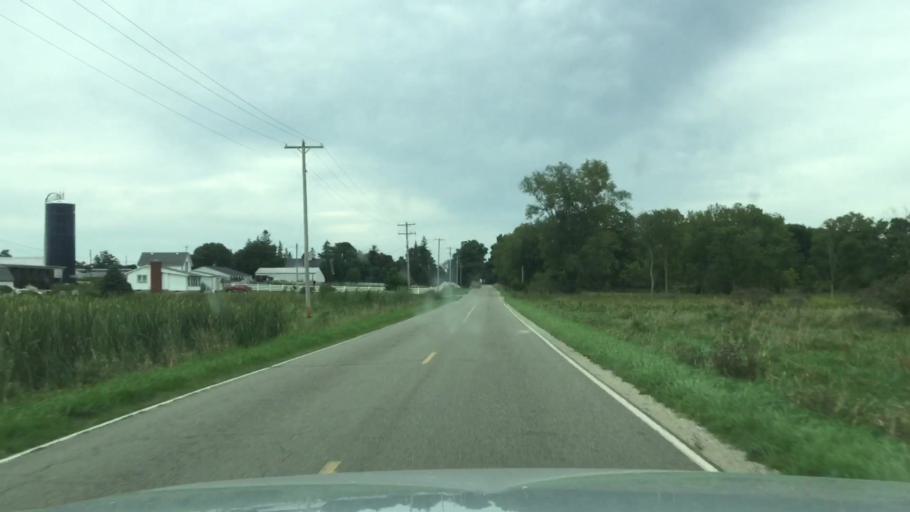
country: US
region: Michigan
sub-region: Shiawassee County
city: Durand
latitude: 42.8231
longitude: -83.9906
